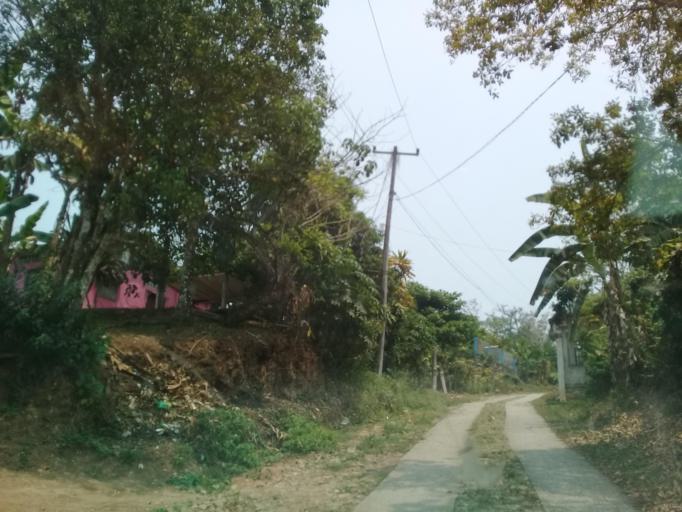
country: MX
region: Veracruz
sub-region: Tezonapa
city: Laguna Chica (Pueblo Nuevo)
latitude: 18.5475
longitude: -96.7358
